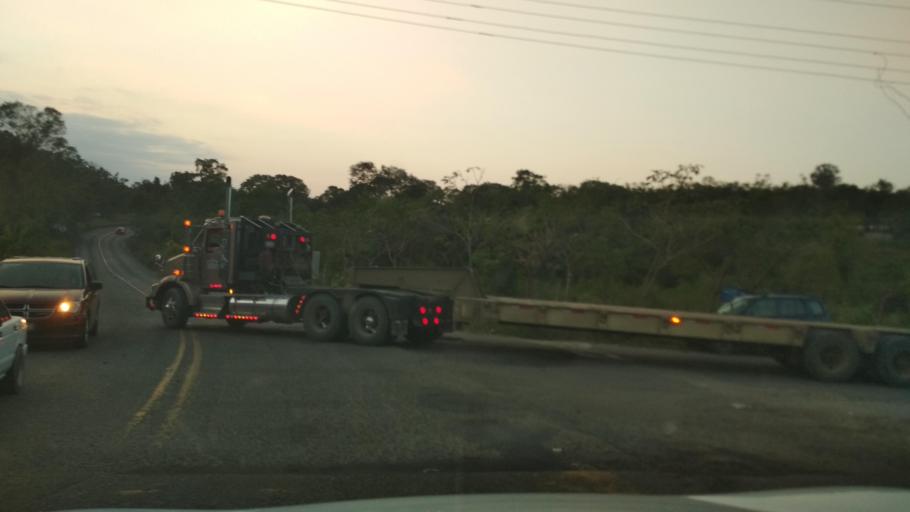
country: MX
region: Veracruz
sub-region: Poza Rica de Hidalgo
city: Arroyo del Maiz Uno
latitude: 20.4792
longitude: -97.3863
